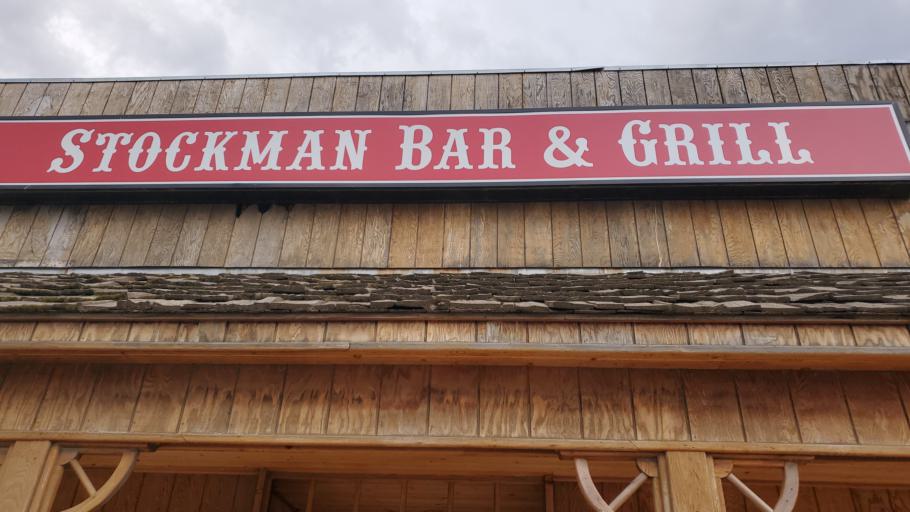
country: US
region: Montana
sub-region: Phillips County
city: Malta
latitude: 48.3596
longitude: -107.8724
